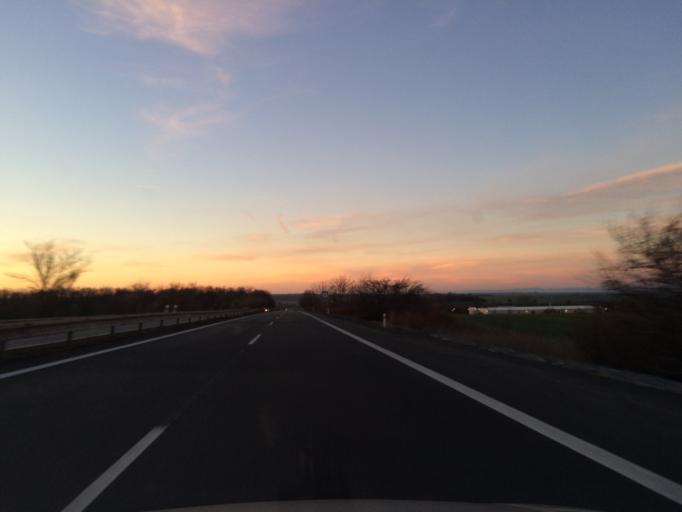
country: CZ
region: Central Bohemia
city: Tuchomerice
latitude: 50.1346
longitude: 14.2505
